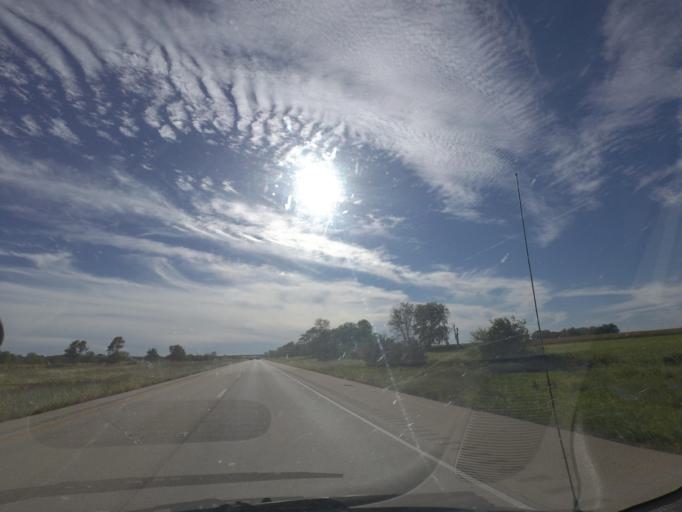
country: US
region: Illinois
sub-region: Macon County
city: Forsyth
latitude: 39.9232
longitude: -88.8542
